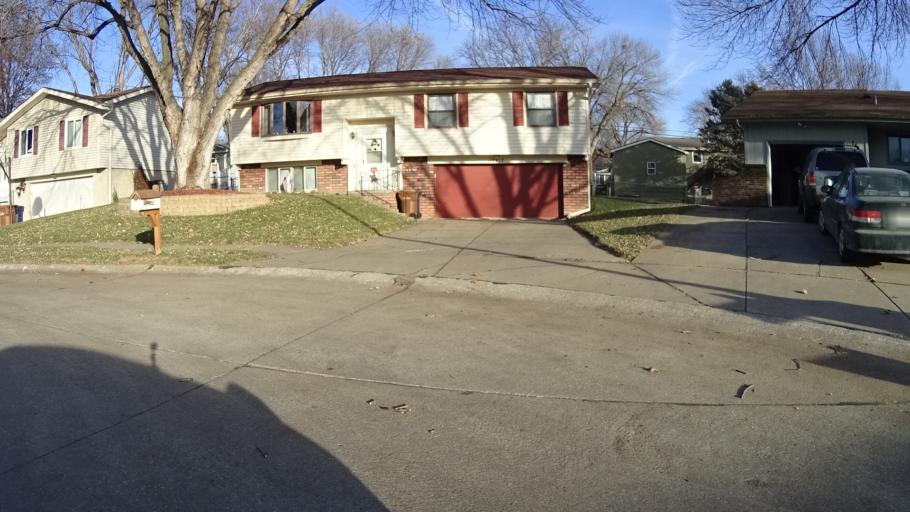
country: US
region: Nebraska
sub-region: Sarpy County
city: La Vista
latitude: 41.1851
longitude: -95.9978
